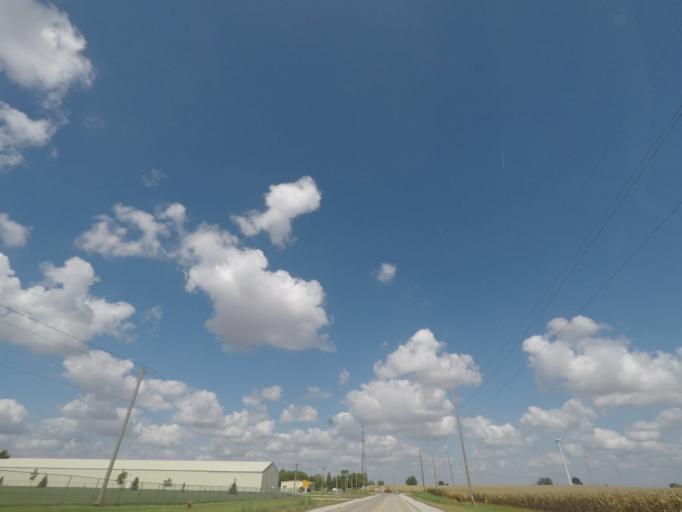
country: US
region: Iowa
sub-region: Story County
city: Nevada
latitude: 42.0206
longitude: -93.4346
